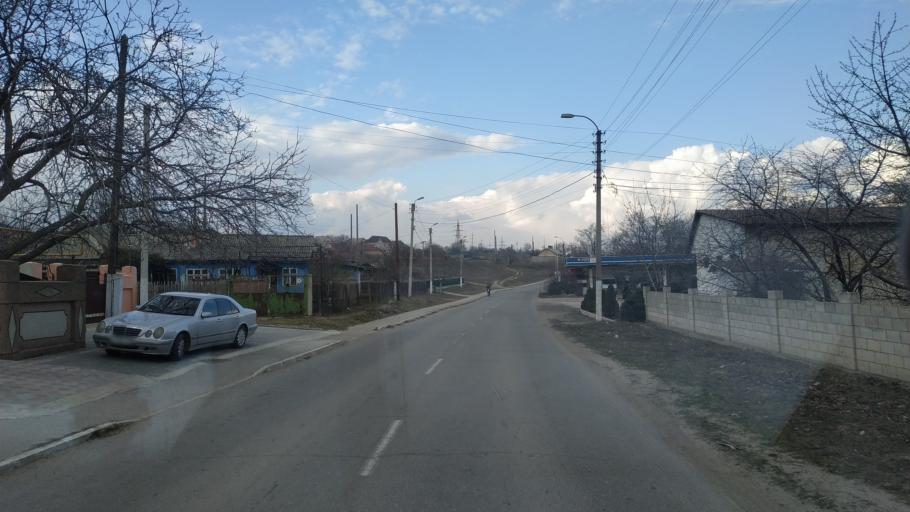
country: MD
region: Anenii Noi
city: Varnita
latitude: 46.8672
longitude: 29.4754
